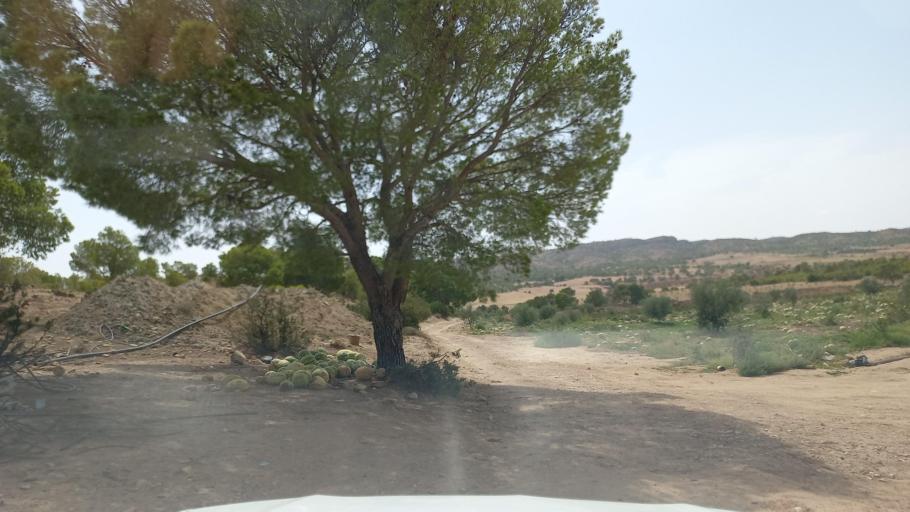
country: TN
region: Al Qasrayn
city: Sbiba
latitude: 35.3940
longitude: 8.9869
